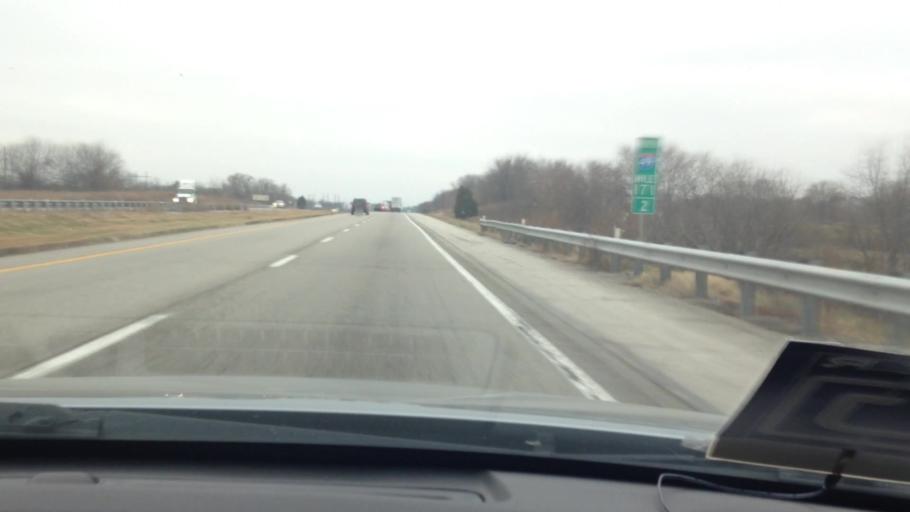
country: US
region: Missouri
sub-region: Cass County
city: Raymore
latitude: 38.7712
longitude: -94.4918
